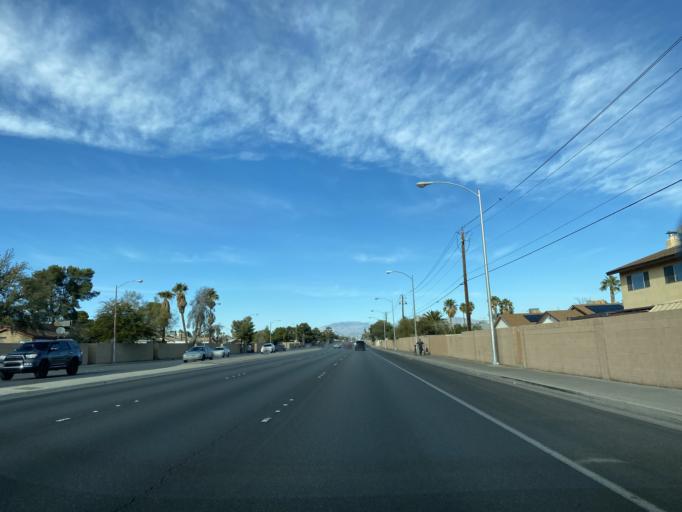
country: US
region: Nevada
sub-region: Clark County
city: Spring Valley
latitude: 36.1165
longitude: -115.2428
